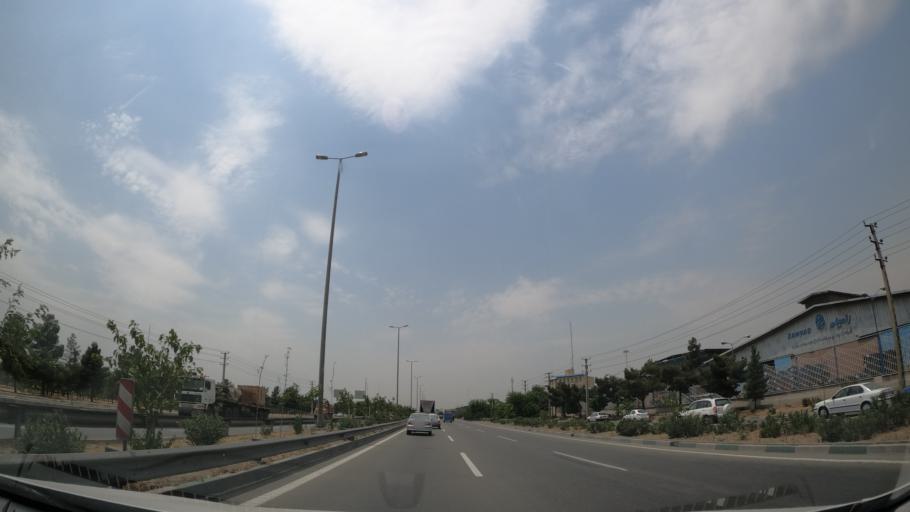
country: IR
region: Tehran
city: Shahr-e Qods
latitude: 35.7050
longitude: 51.1783
